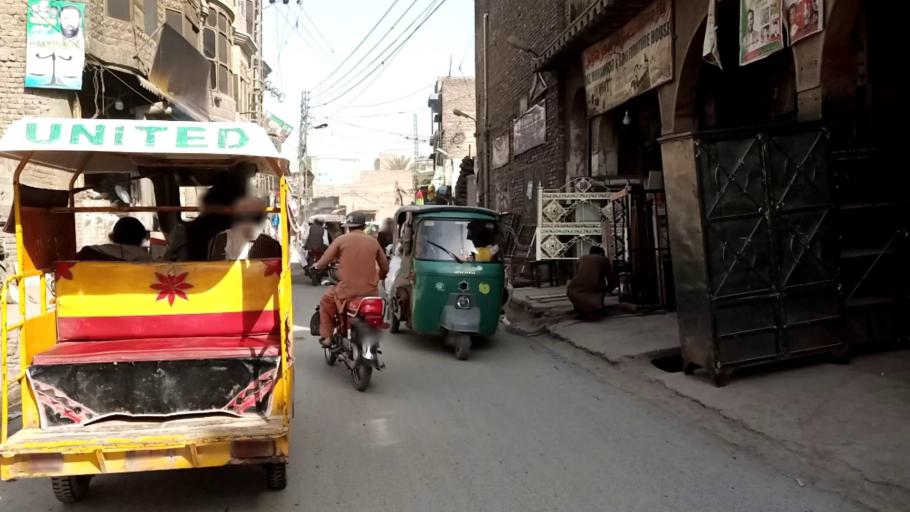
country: PK
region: Khyber Pakhtunkhwa
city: Peshawar
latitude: 34.0032
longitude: 71.5782
